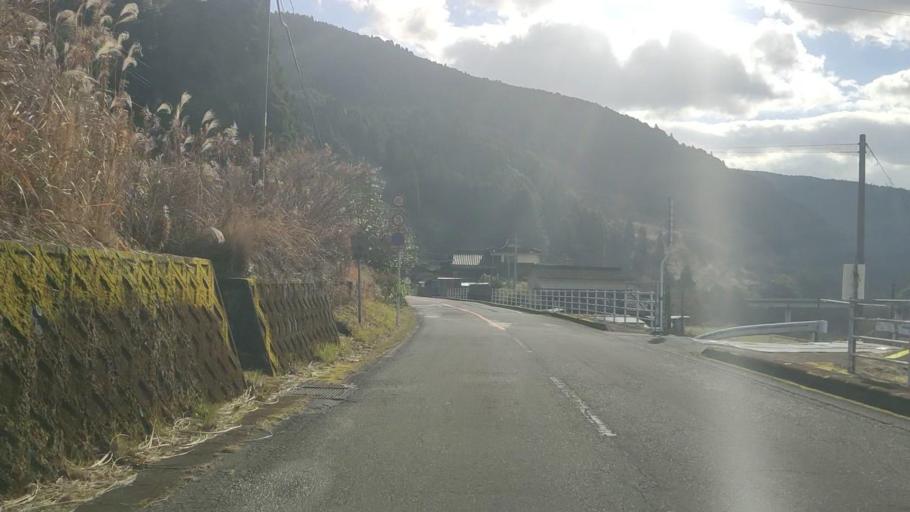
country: JP
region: Kumamoto
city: Hitoyoshi
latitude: 32.3152
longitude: 130.8457
